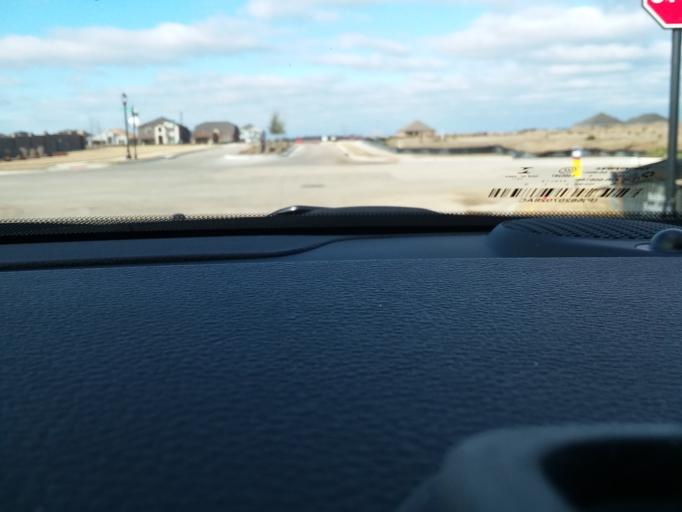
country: US
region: Texas
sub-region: Collin County
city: Prosper
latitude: 33.2674
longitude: -96.8872
